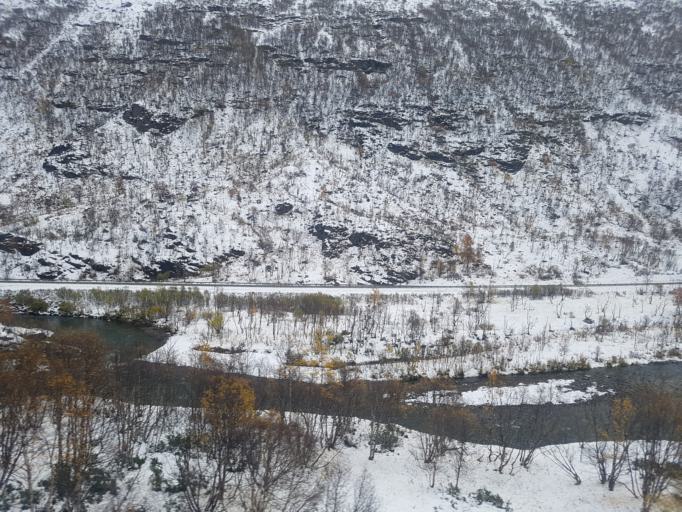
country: NO
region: Sor-Trondelag
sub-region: Oppdal
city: Oppdal
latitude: 62.3345
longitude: 9.6223
